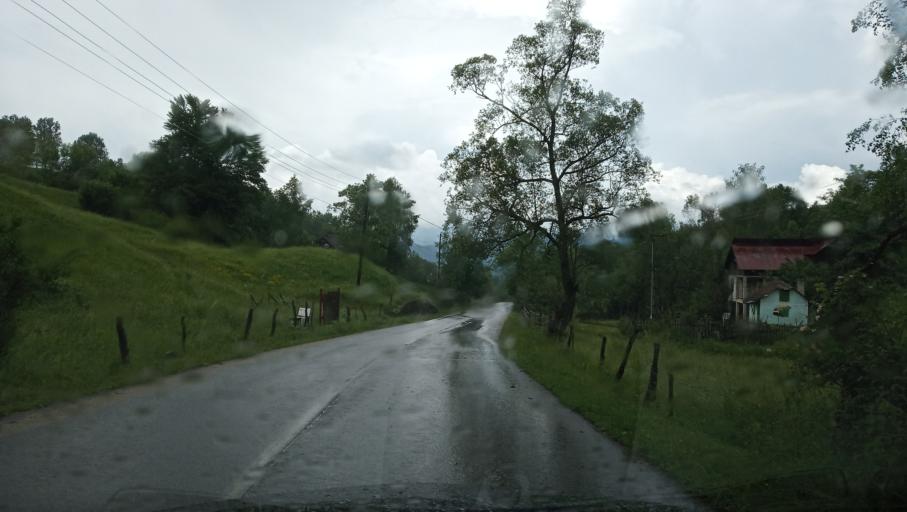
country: RO
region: Hunedoara
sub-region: Oras Petrila
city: Petrila
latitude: 45.4000
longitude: 23.4162
